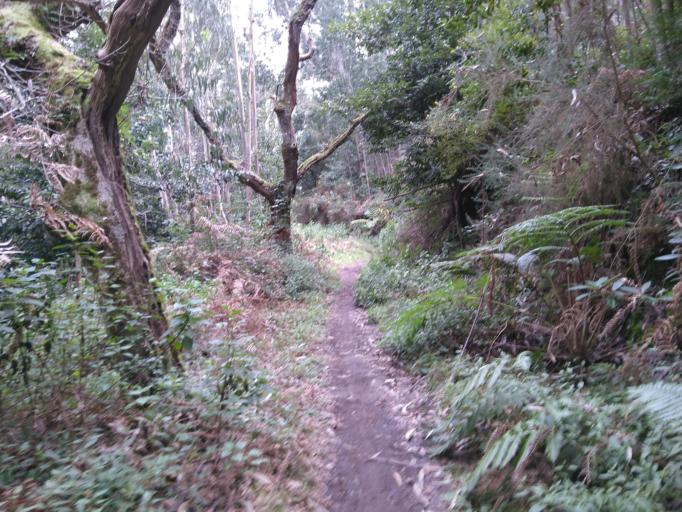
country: PT
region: Madeira
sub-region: Santa Cruz
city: Camacha
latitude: 32.7188
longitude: -16.8406
